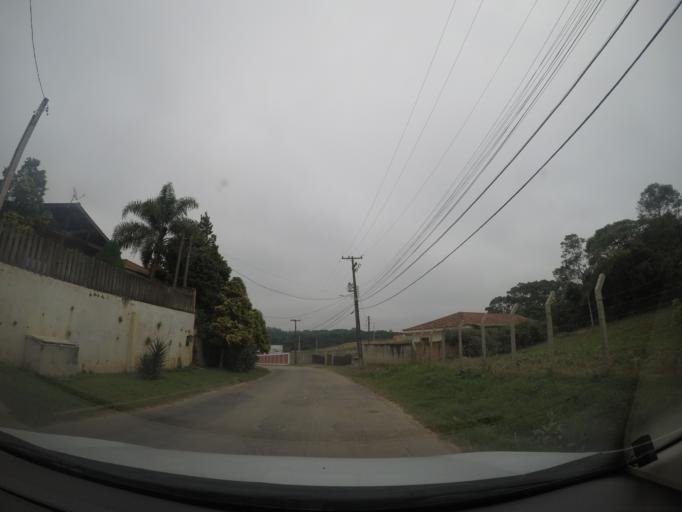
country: BR
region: Parana
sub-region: Colombo
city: Colombo
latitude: -25.3289
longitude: -49.2506
